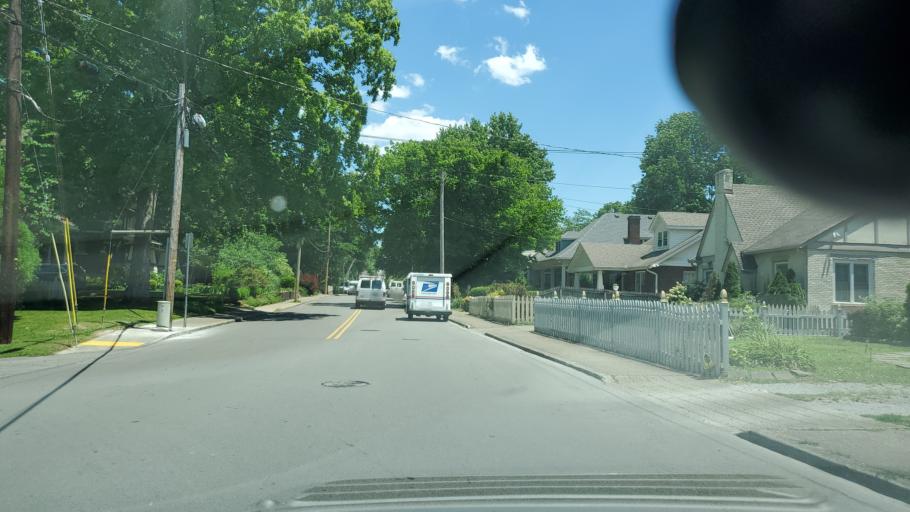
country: US
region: Tennessee
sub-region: Davidson County
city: Nashville
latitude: 36.1899
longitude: -86.7420
